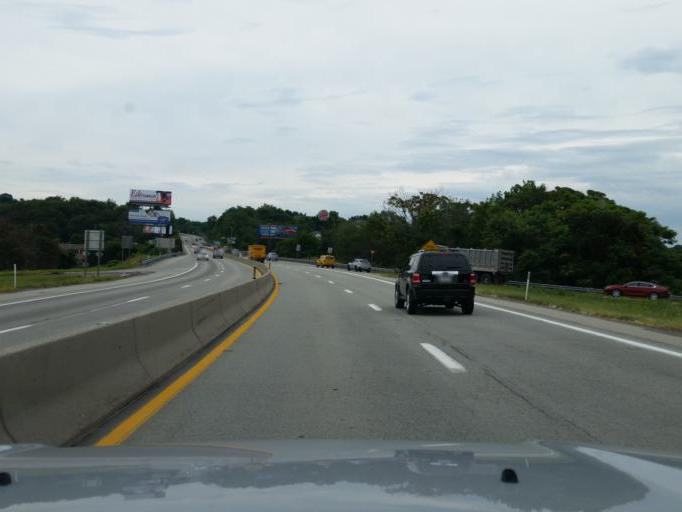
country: US
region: Pennsylvania
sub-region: Westmoreland County
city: Southwest Greensburg
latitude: 40.2871
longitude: -79.5497
